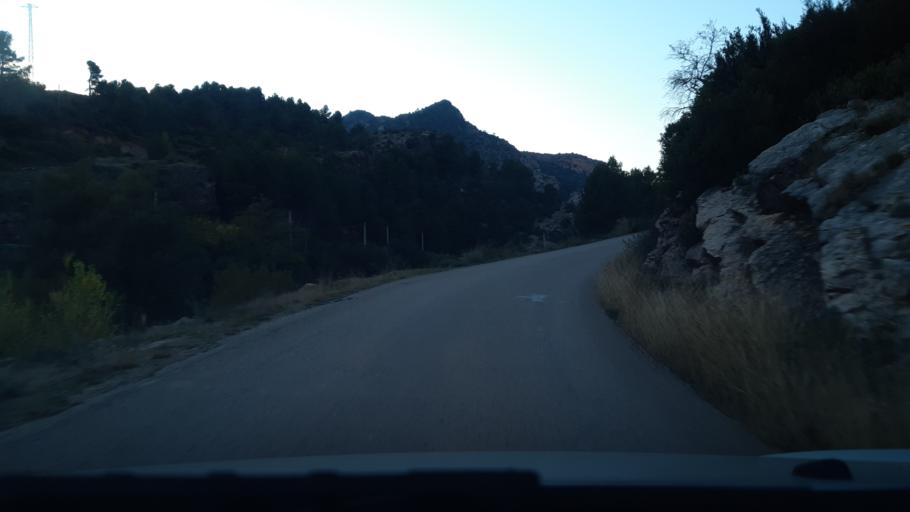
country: ES
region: Aragon
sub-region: Provincia de Teruel
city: Valderrobres
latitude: 40.8396
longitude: 0.1852
